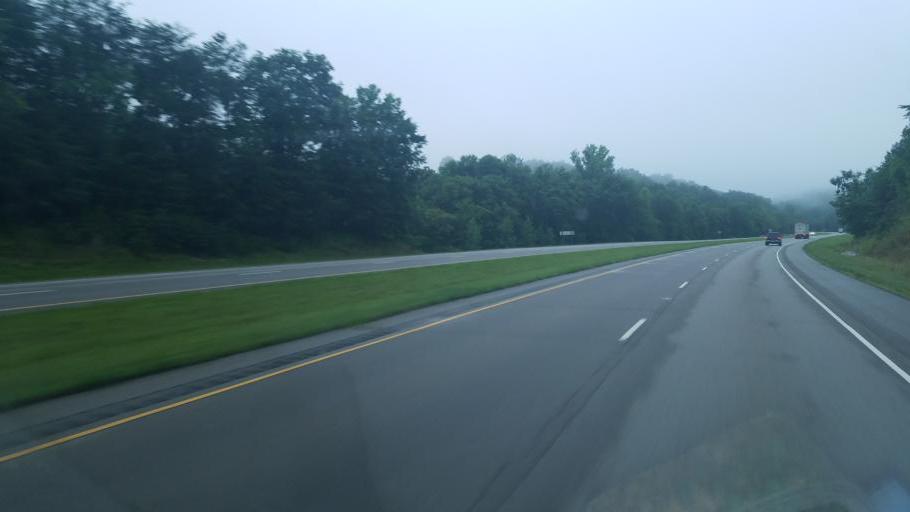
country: US
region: Ohio
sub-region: Jackson County
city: Oak Hill
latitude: 38.9340
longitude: -82.4681
